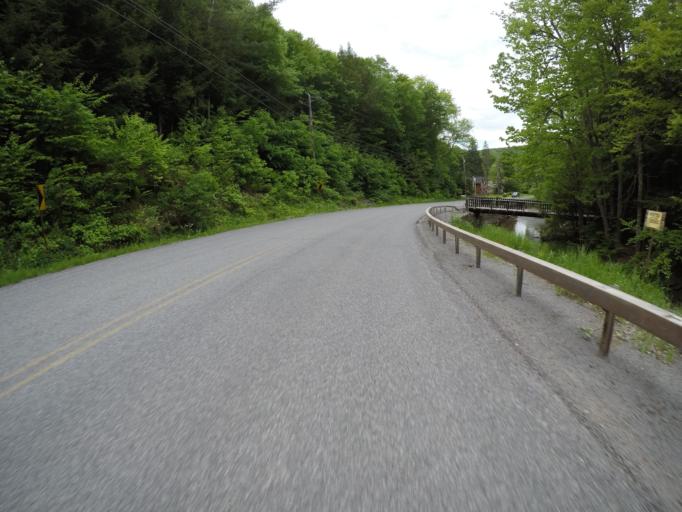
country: US
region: New York
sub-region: Delaware County
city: Stamford
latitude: 42.1809
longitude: -74.5948
